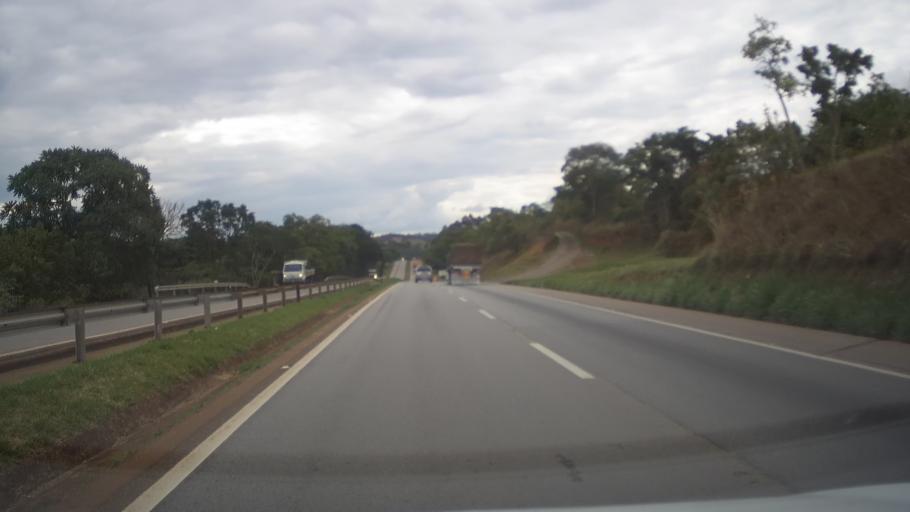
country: BR
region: Minas Gerais
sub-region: Itauna
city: Itauna
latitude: -20.3342
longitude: -44.4484
